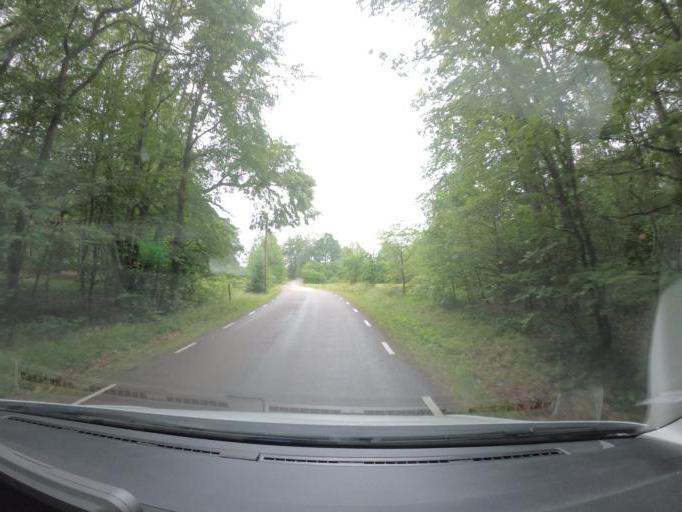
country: SE
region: Skane
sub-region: Orkelljunga Kommun
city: OErkelljunga
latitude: 56.2606
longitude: 13.1569
